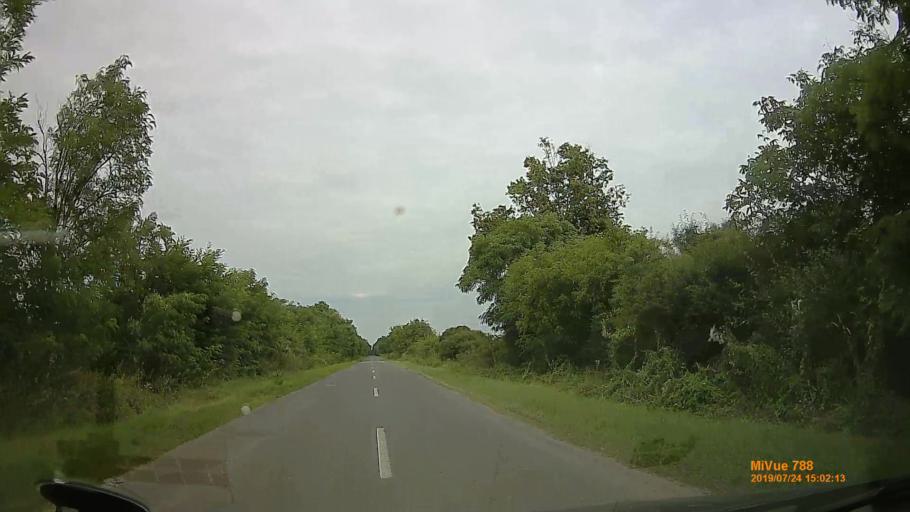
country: HU
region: Szabolcs-Szatmar-Bereg
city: Vasarosnameny
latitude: 48.2257
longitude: 22.4026
